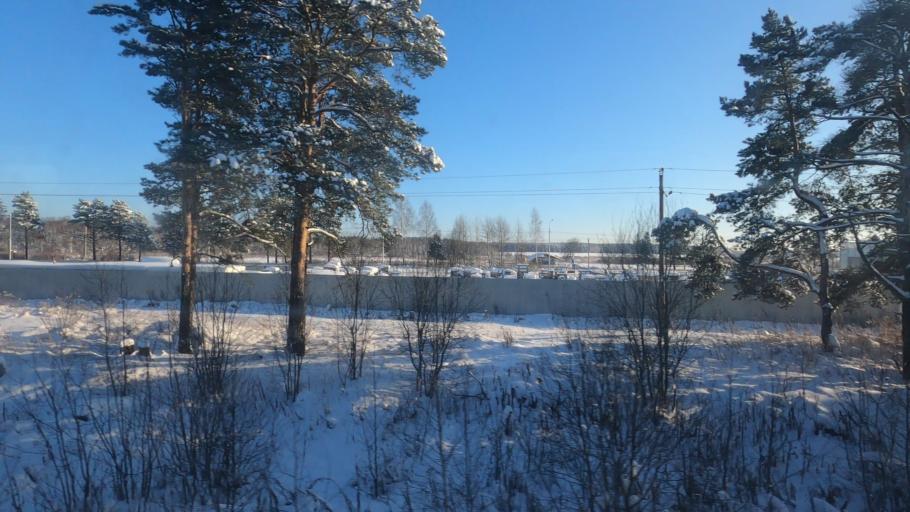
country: RU
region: Moskovskaya
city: Orud'yevo
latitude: 56.4505
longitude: 37.5251
